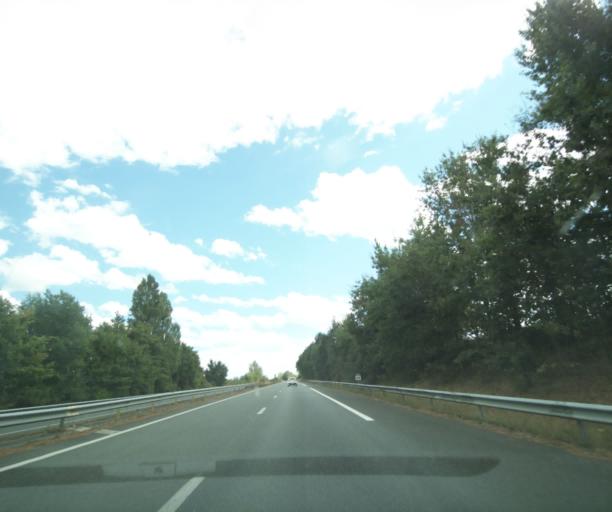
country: FR
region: Aquitaine
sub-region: Departement du Lot-et-Garonne
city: Meilhan-sur-Garonne
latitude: 44.4879
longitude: 0.0051
